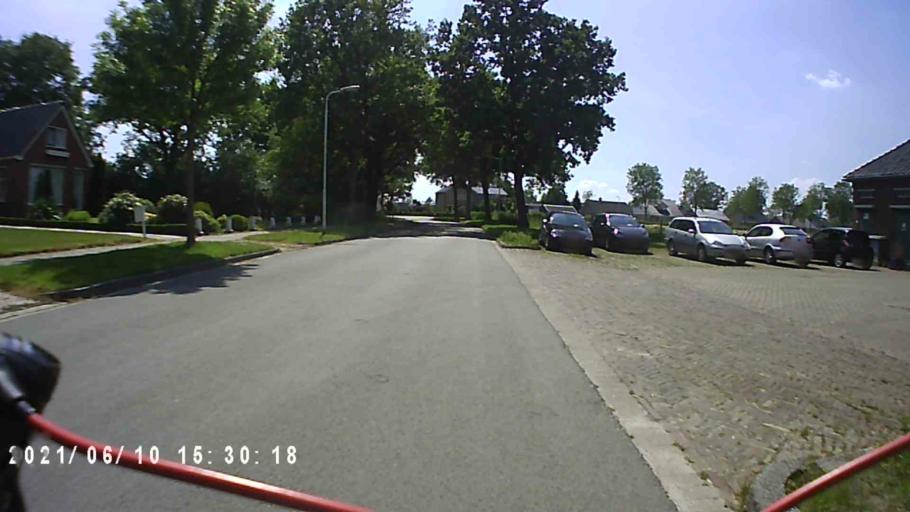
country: NL
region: Friesland
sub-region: Gemeente Achtkarspelen
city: Surhuisterveen
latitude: 53.1783
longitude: 6.1747
